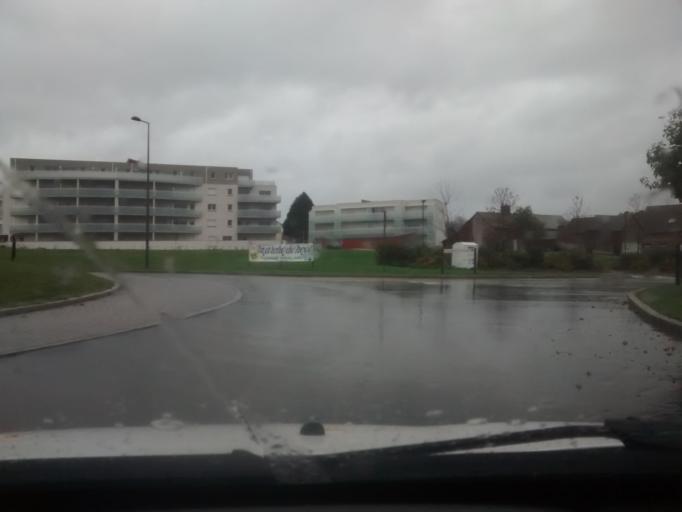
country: FR
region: Brittany
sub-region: Departement d'Ille-et-Vilaine
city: Fouillard
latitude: 48.1512
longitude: -1.5787
